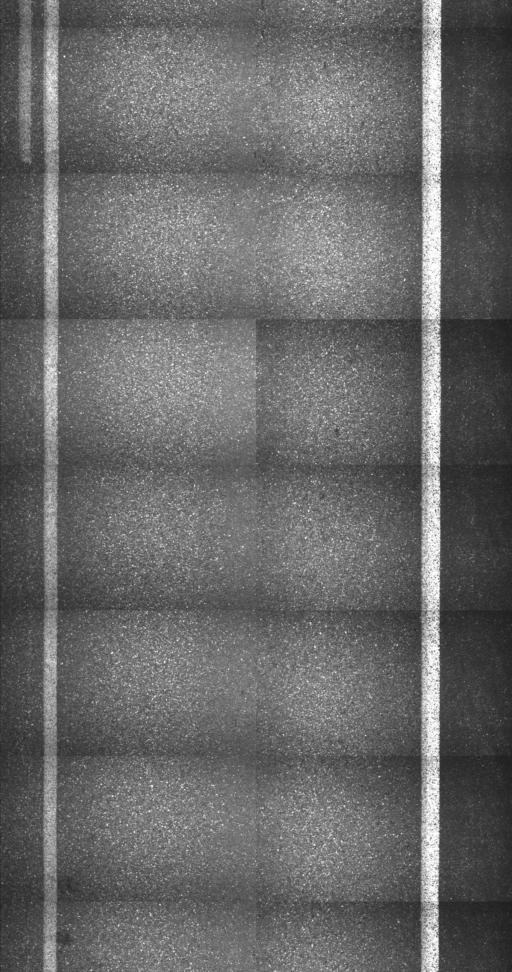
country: US
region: Vermont
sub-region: Orleans County
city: Newport
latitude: 44.8786
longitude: -71.9607
